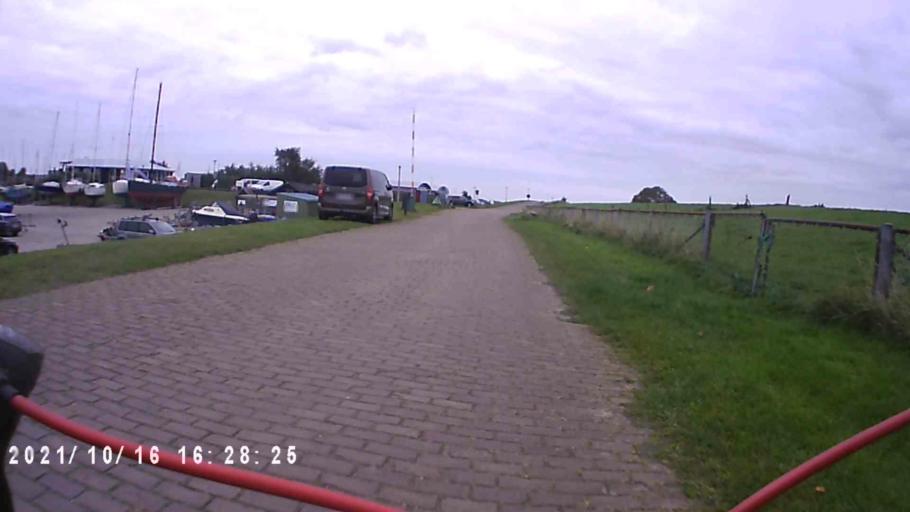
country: NL
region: Friesland
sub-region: Gemeente Dongeradeel
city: Anjum
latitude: 53.3820
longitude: 6.1557
